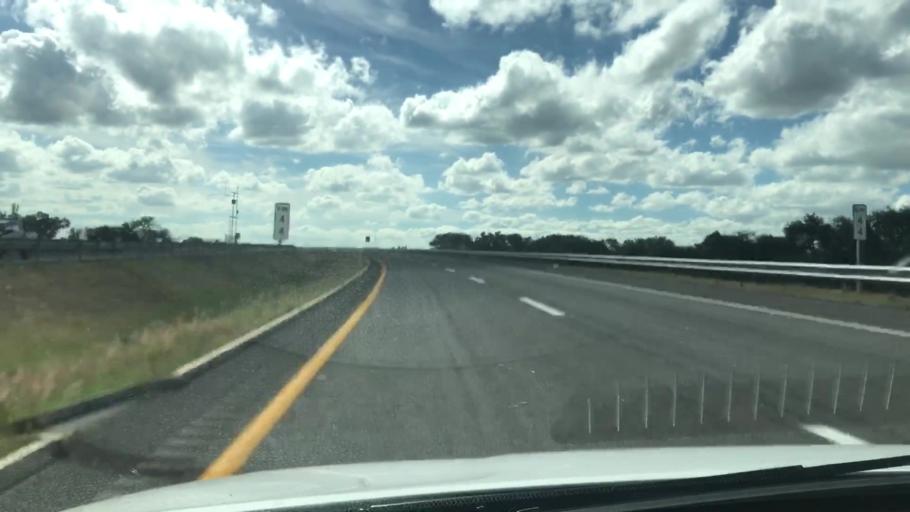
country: MX
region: Guanajuato
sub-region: Leon
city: San Antonio de los Tepetates
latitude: 21.0241
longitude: -101.6134
